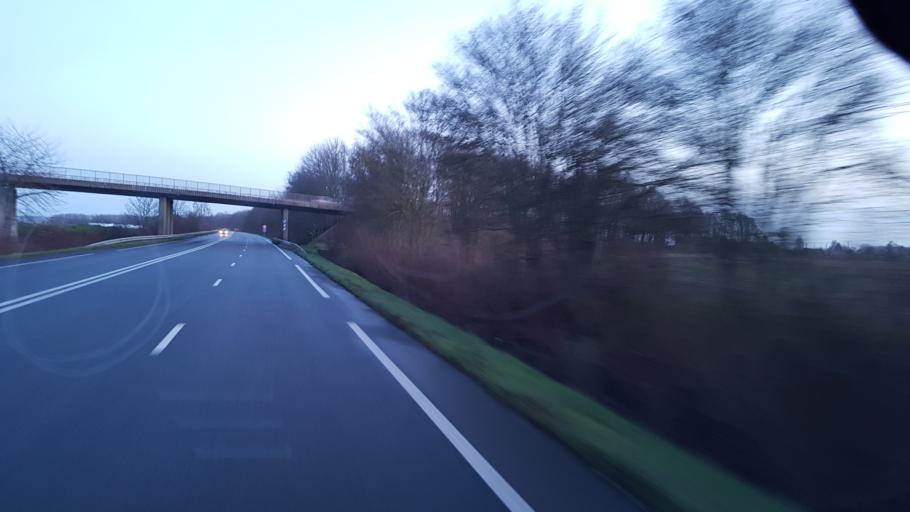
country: FR
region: Nord-Pas-de-Calais
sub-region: Departement du Nord
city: Goeulzin
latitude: 50.3328
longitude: 3.0939
